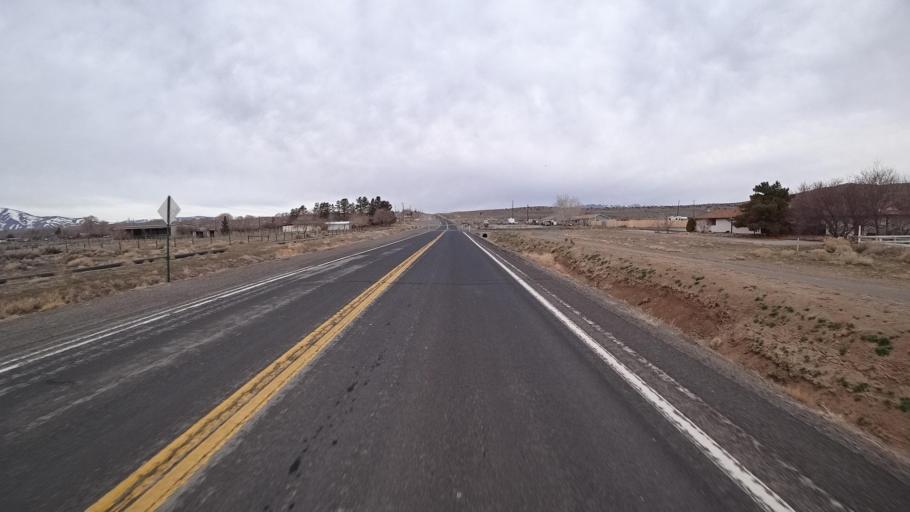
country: US
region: Nevada
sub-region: Washoe County
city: Lemmon Valley
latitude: 39.6748
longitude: -119.8463
